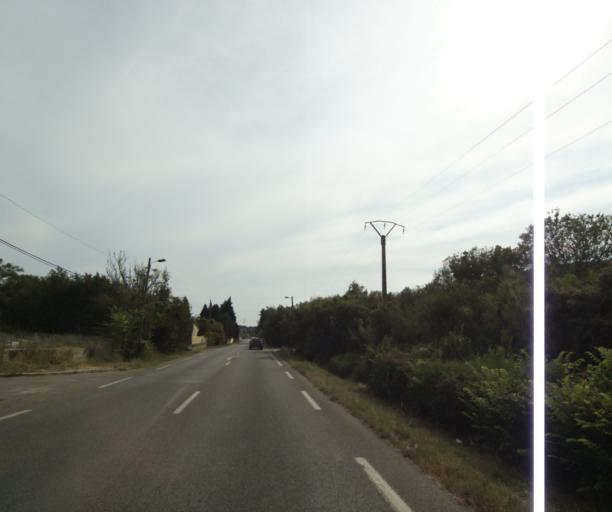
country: FR
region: Provence-Alpes-Cote d'Azur
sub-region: Departement du Var
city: La Farlede
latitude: 43.1504
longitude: 6.0333
